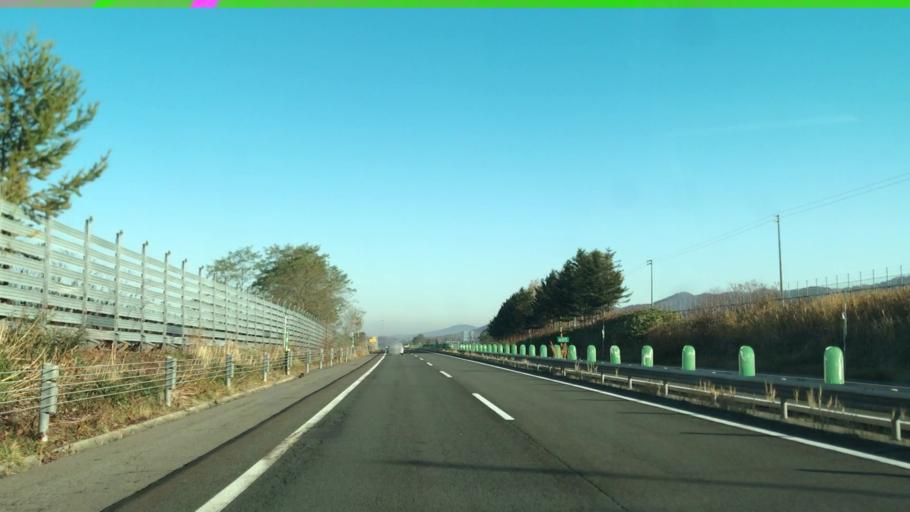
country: JP
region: Hokkaido
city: Sunagawa
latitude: 43.4346
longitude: 141.9153
